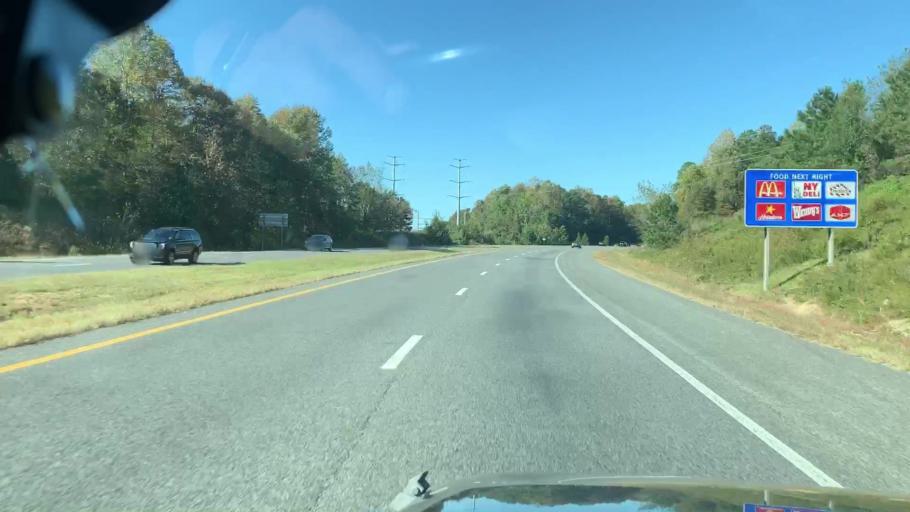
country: US
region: Virginia
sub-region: James City County
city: Williamsburg
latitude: 37.3247
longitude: -76.7547
